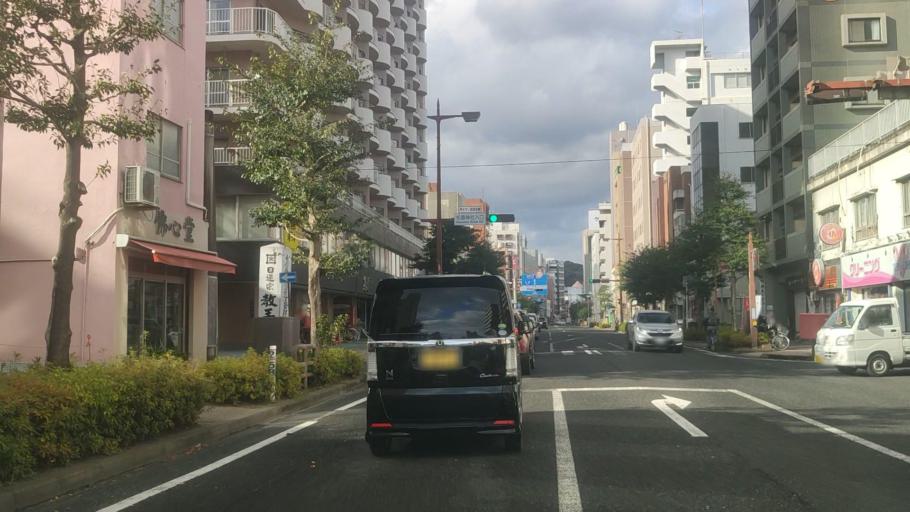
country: JP
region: Kagoshima
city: Kagoshima-shi
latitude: 31.5872
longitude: 130.5589
